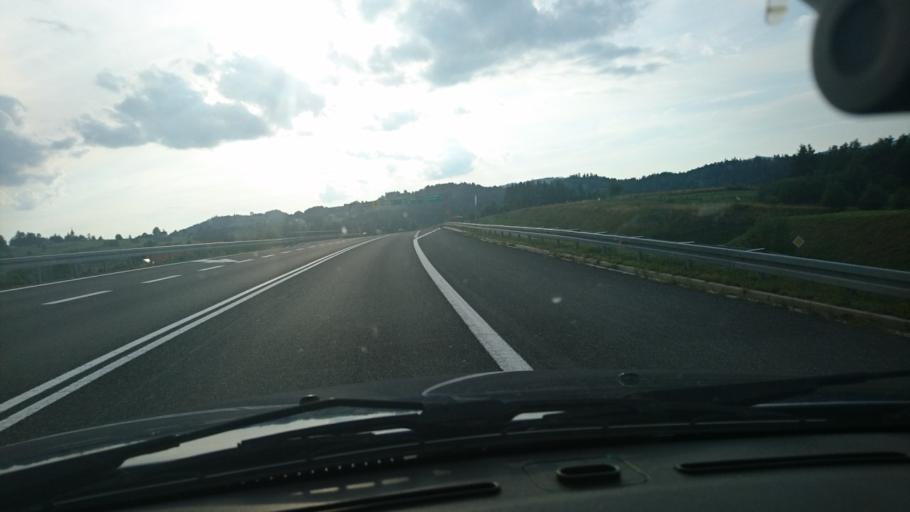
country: PL
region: Silesian Voivodeship
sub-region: Powiat zywiecki
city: Kamesznica
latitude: 49.5481
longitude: 19.0303
